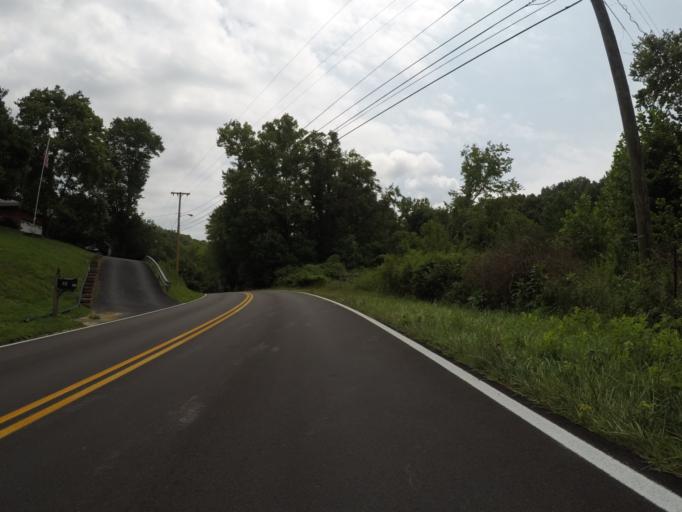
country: US
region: Kentucky
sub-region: Boyd County
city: Ashland
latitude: 38.4370
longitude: -82.6295
